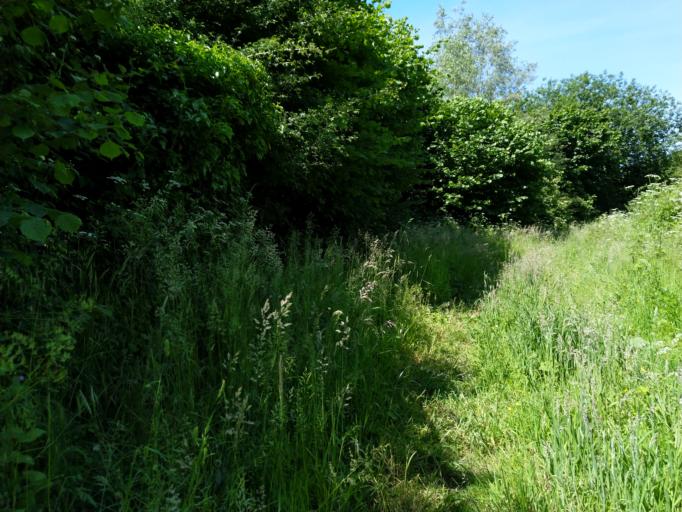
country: BE
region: Wallonia
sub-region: Province du Hainaut
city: Mons
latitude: 50.4638
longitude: 3.9906
